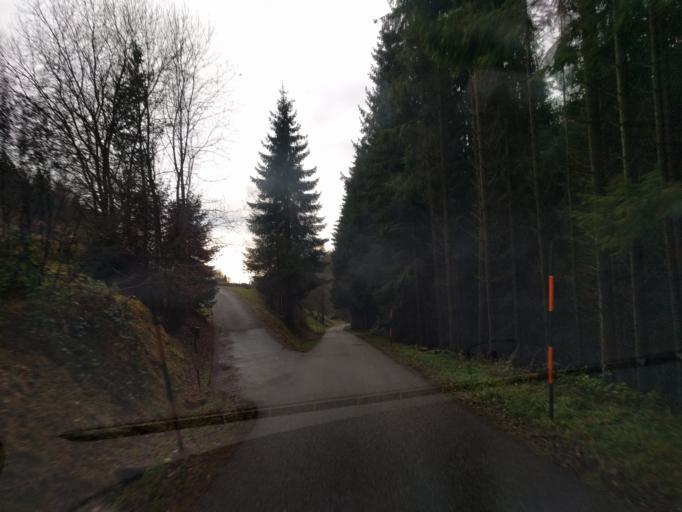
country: AT
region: Upper Austria
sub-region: Politischer Bezirk Urfahr-Umgebung
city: Hellmonsodt
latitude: 48.4160
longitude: 14.2956
